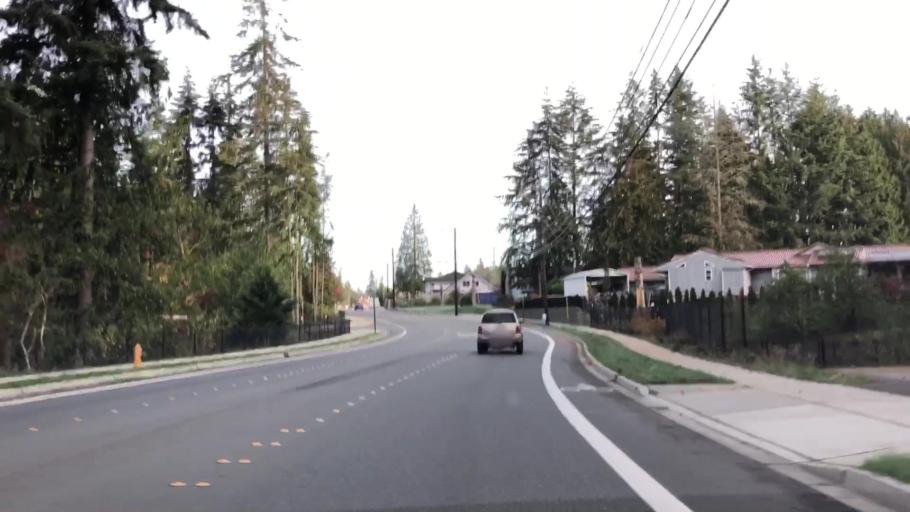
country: US
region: Washington
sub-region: Snohomish County
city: Martha Lake
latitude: 47.8428
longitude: -122.2357
